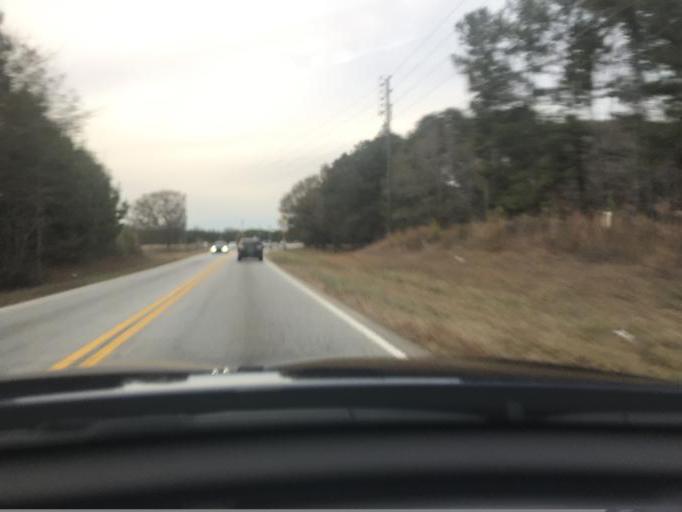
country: US
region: Georgia
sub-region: Newton County
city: Porterdale
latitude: 33.5956
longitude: -83.9152
